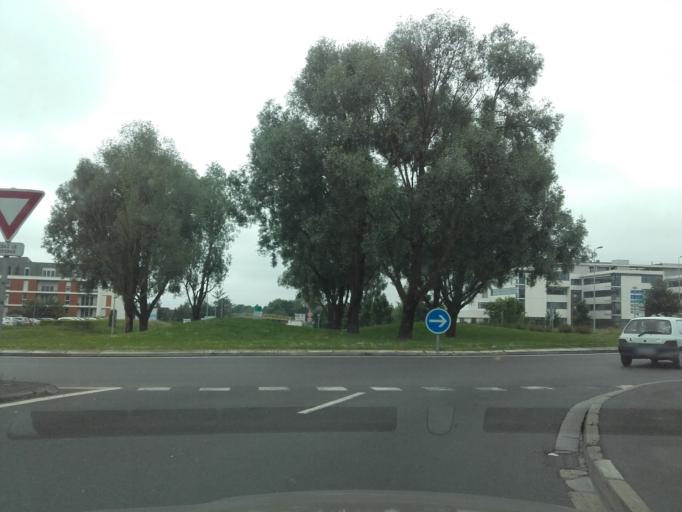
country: FR
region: Centre
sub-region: Departement d'Indre-et-Loire
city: Chanceaux-sur-Choisille
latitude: 47.4301
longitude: 0.7054
